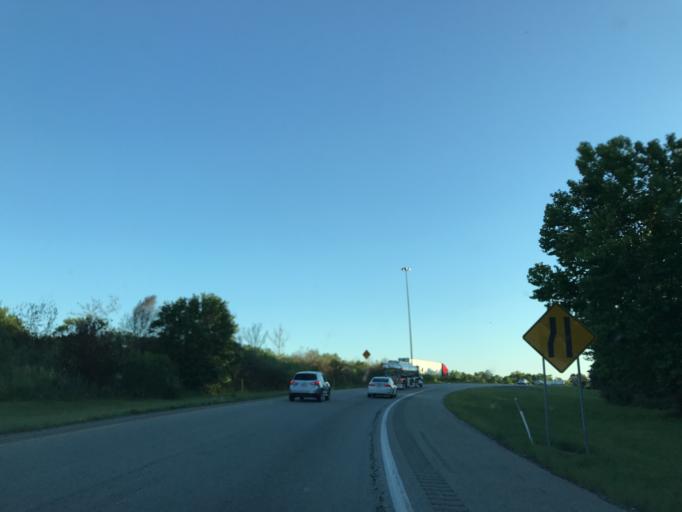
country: US
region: Pennsylvania
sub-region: Delaware County
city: Eddystone
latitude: 39.8674
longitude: -75.3453
